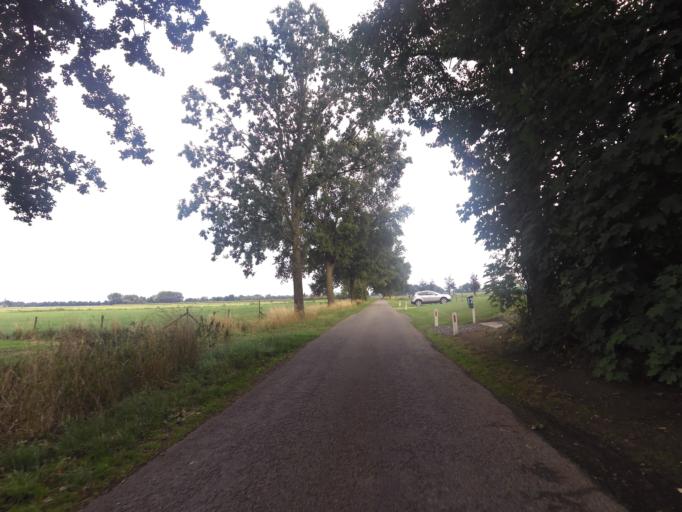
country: NL
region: Gelderland
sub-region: Oude IJsselstreek
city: Gendringen
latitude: 51.9044
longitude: 6.3325
